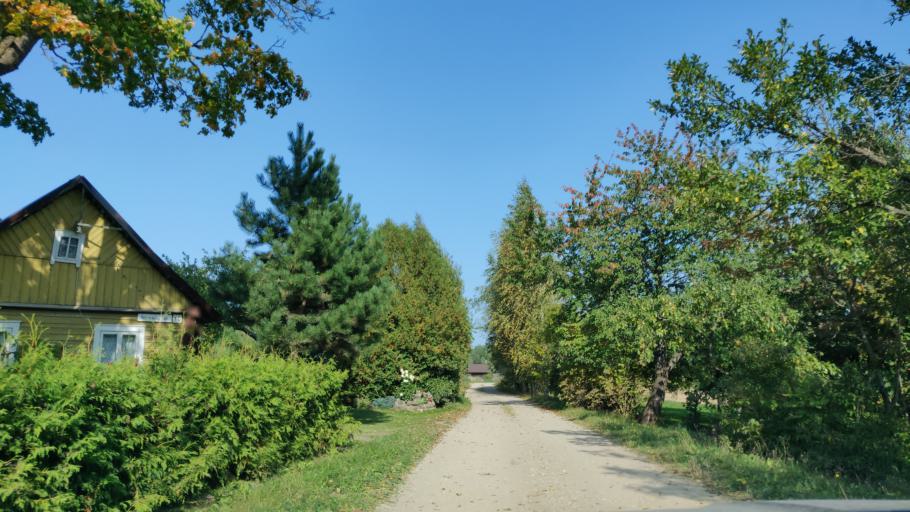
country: LT
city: Sirvintos
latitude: 54.9623
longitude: 24.7847
